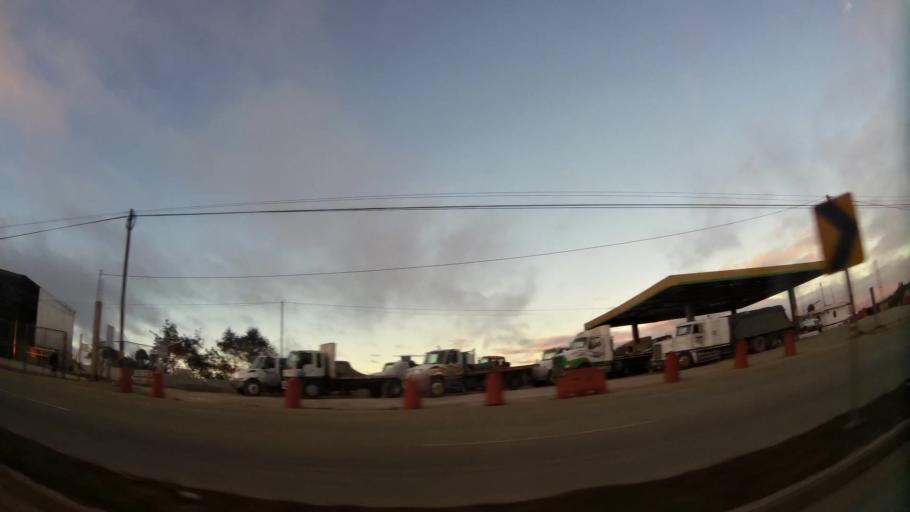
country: GT
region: Solola
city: Concepcion
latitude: 14.8377
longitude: -91.1165
